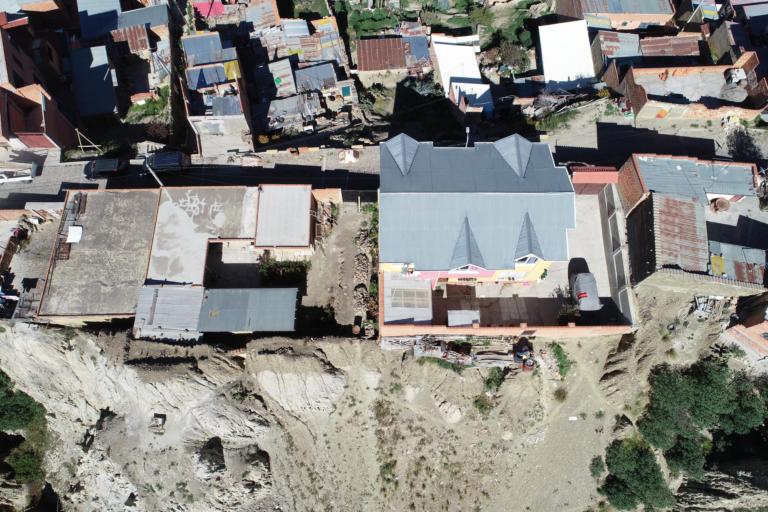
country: BO
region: La Paz
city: La Paz
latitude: -16.5248
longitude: -68.0944
